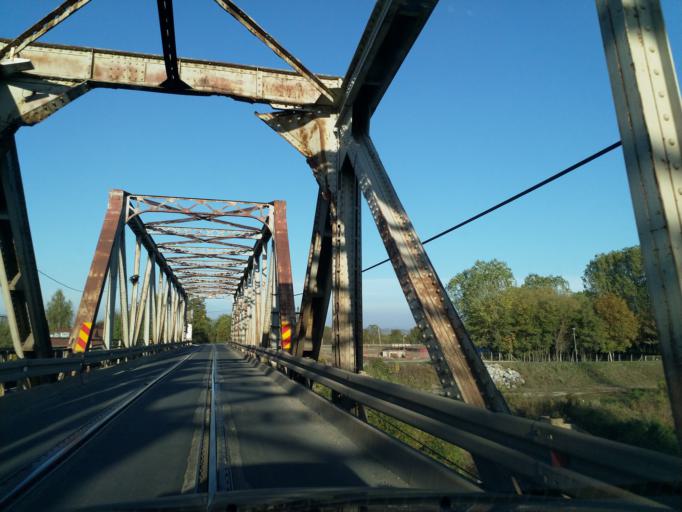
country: RS
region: Central Serbia
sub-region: Pomoravski Okrug
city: Svilajnac
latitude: 44.2250
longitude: 21.1539
